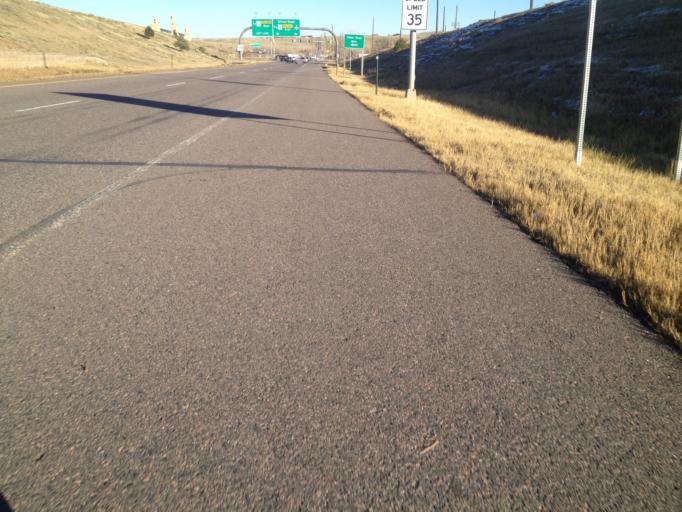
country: US
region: Colorado
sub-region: Boulder County
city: Lafayette
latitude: 39.9580
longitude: -105.0934
